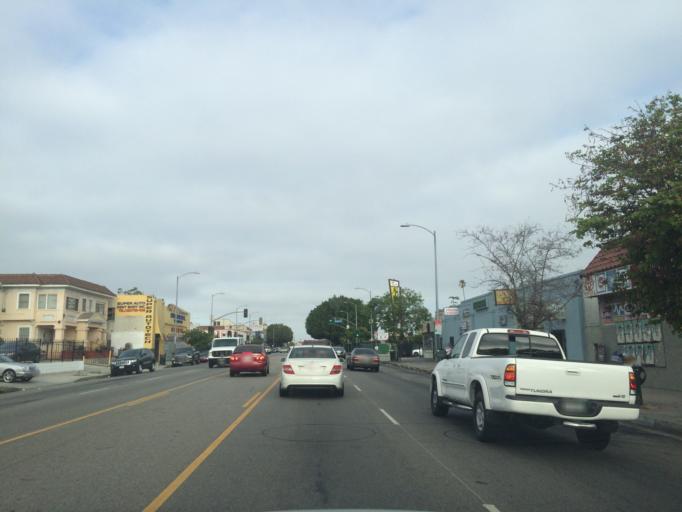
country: US
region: California
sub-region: Los Angeles County
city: View Park-Windsor Hills
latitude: 34.0400
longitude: -118.3119
